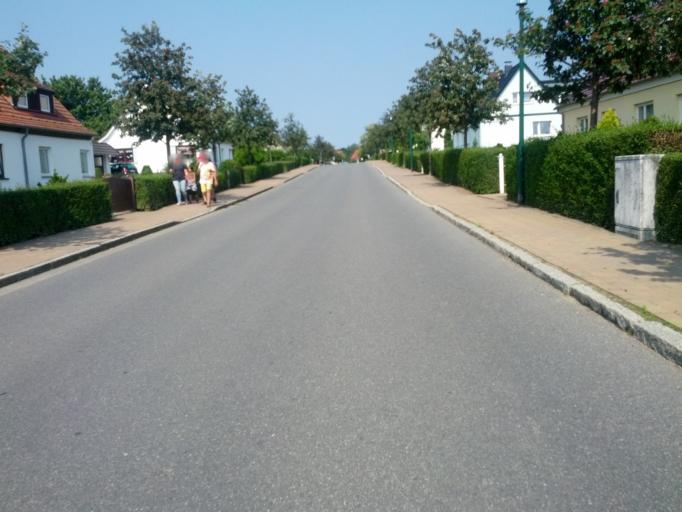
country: DE
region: Mecklenburg-Vorpommern
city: Bastorf
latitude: 54.1045
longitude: 11.6211
